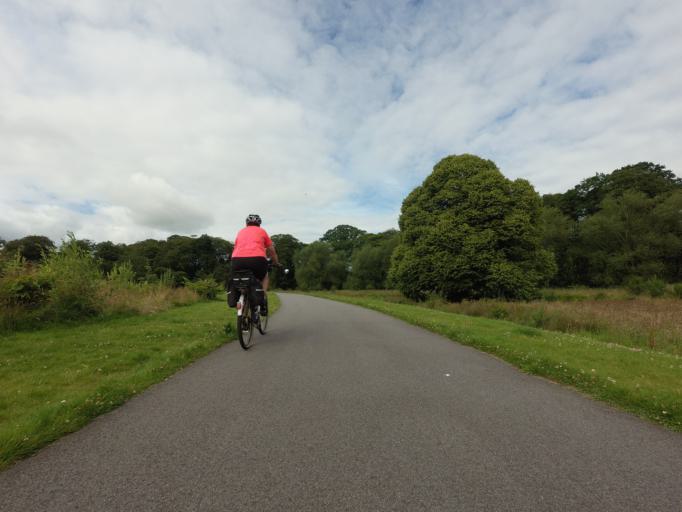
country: GB
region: Scotland
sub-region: Moray
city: Elgin
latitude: 57.6526
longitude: -3.3242
